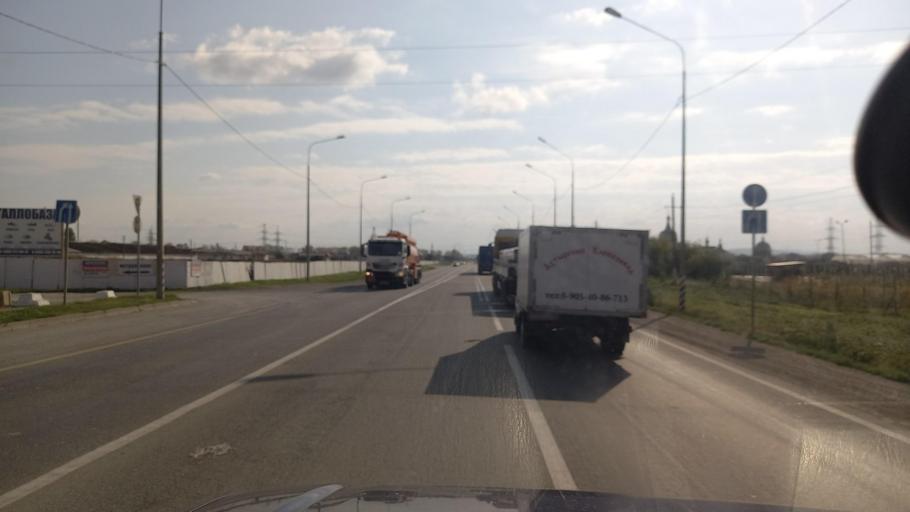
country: RU
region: Krasnodarskiy
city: Novoukrainskiy
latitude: 44.9077
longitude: 38.0244
